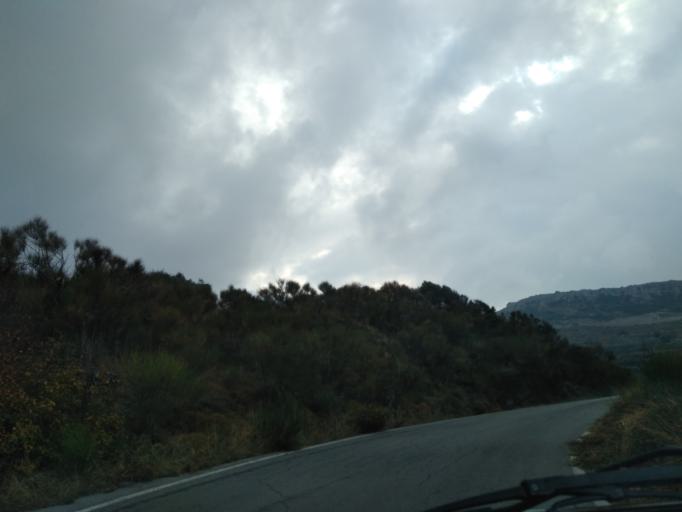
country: GR
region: Crete
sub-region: Nomos Lasithiou
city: Siteia
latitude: 35.1389
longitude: 26.0231
